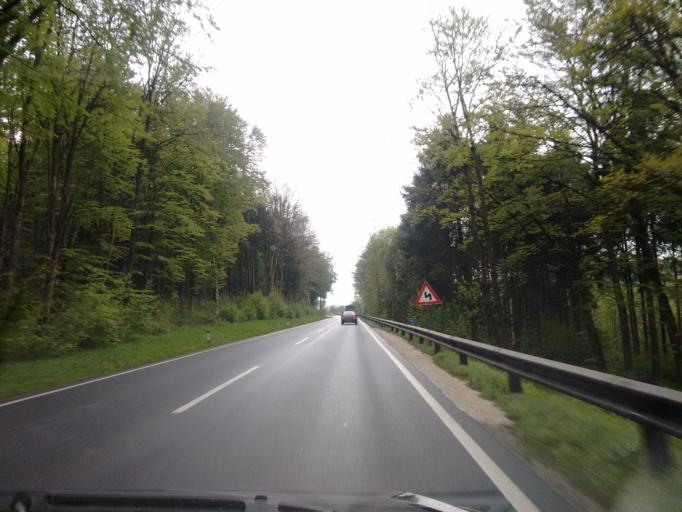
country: AT
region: Upper Austria
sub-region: Politischer Bezirk Vocklabruck
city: Attnang-Puchheim
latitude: 48.0069
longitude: 13.6979
